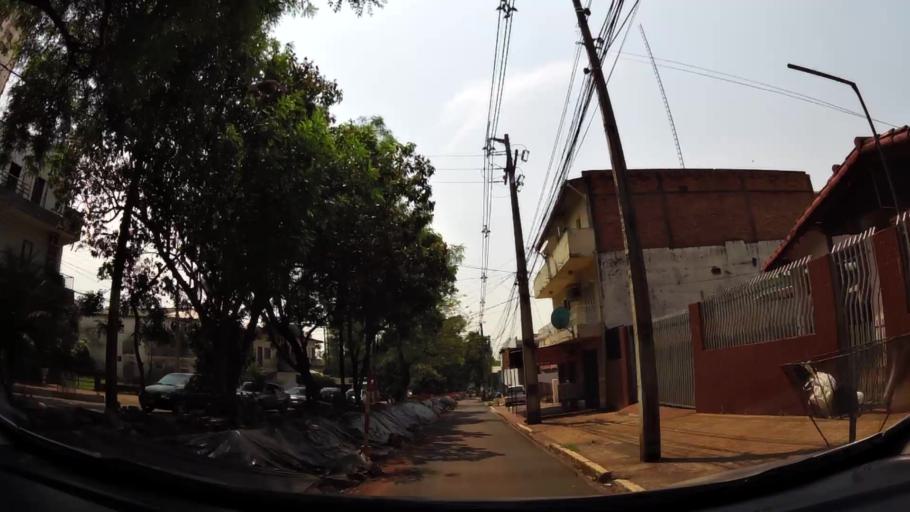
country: PY
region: Alto Parana
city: Ciudad del Este
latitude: -25.5183
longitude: -54.6104
